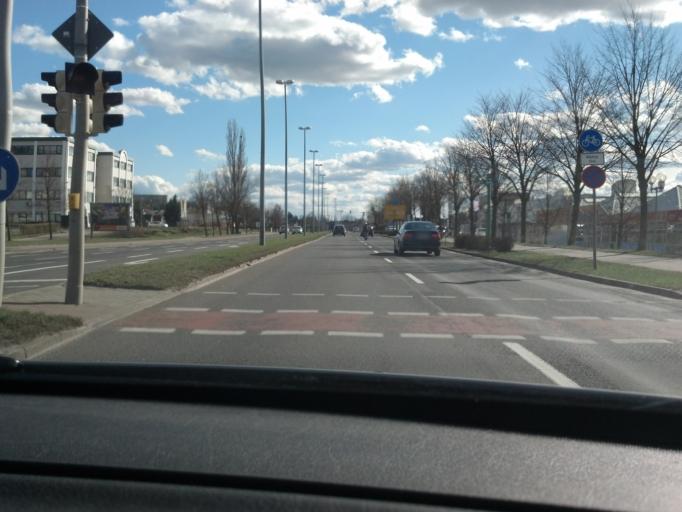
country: DE
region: Mecklenburg-Vorpommern
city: Neubrandenburg
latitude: 53.5824
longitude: 13.2710
